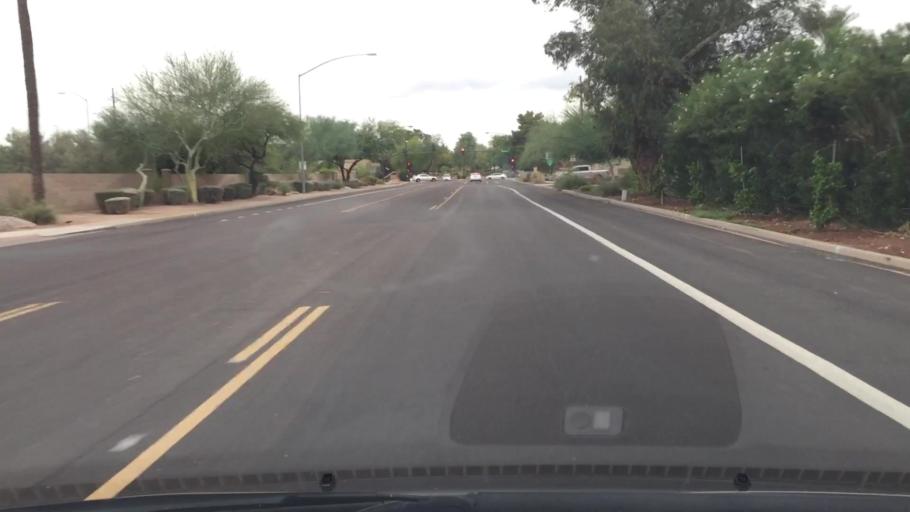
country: US
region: Arizona
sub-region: Maricopa County
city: Gilbert
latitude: 33.3807
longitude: -111.7627
